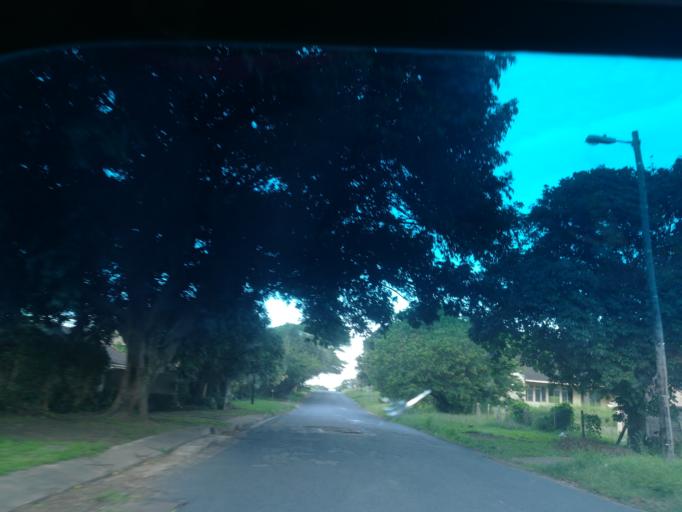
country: ZA
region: KwaZulu-Natal
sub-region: Ugu District Municipality
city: Scottburgh
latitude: -30.2879
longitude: 30.7491
